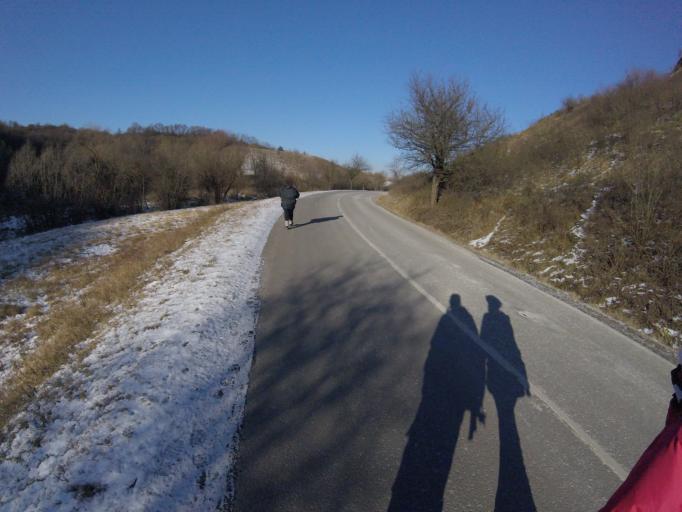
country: HU
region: Nograd
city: Tar
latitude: 47.9918
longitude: 19.7154
